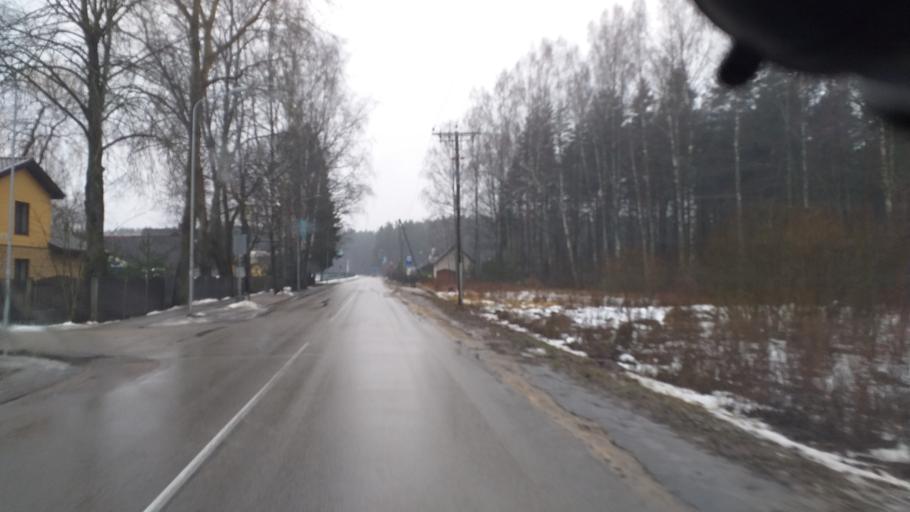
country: LV
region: Babite
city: Pinki
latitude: 56.9651
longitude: 23.9635
